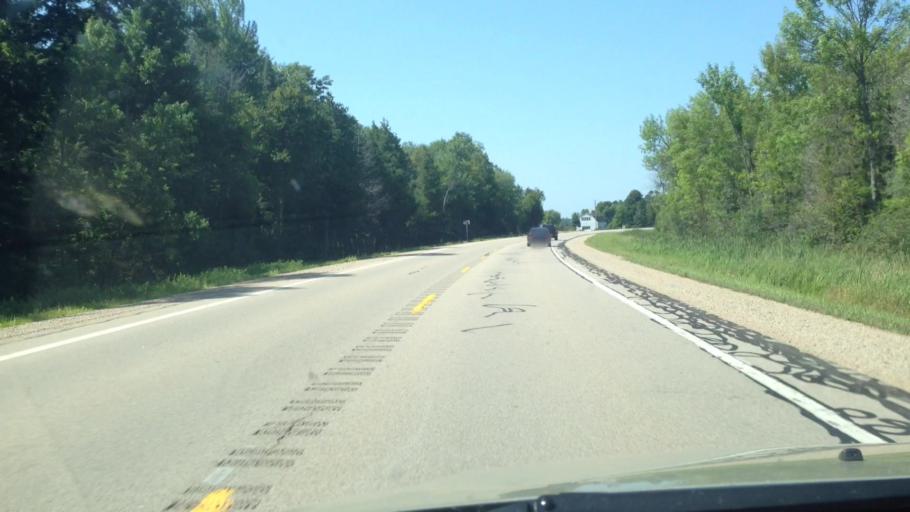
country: US
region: Michigan
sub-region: Menominee County
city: Menominee
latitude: 45.3800
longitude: -87.3773
